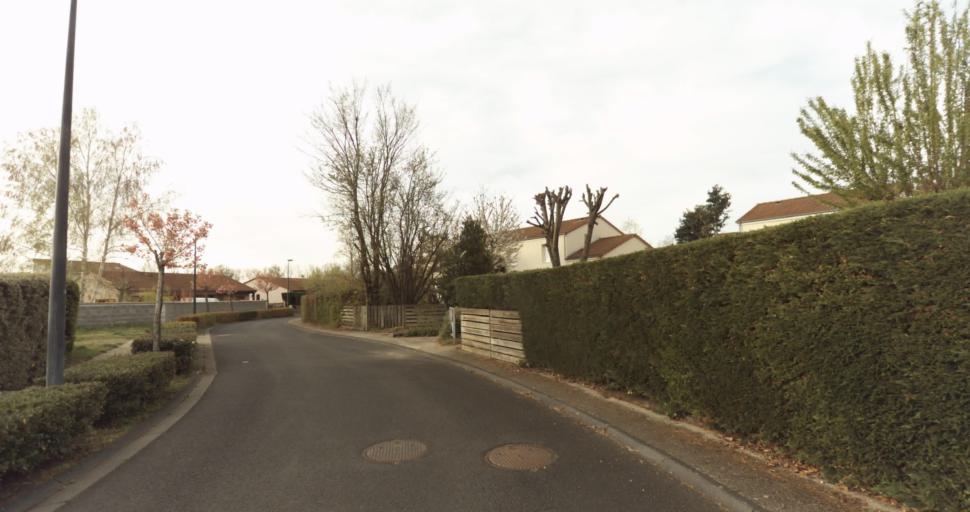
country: FR
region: Auvergne
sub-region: Departement du Puy-de-Dome
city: Cebazat
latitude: 45.8299
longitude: 3.1088
